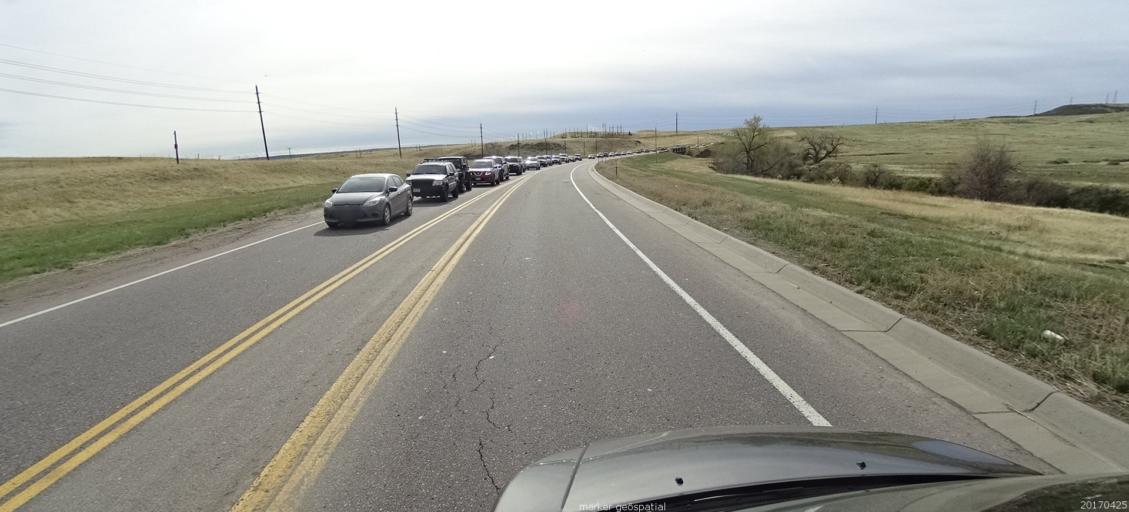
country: US
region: Colorado
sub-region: Douglas County
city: Meridian
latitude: 39.5232
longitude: -104.8566
